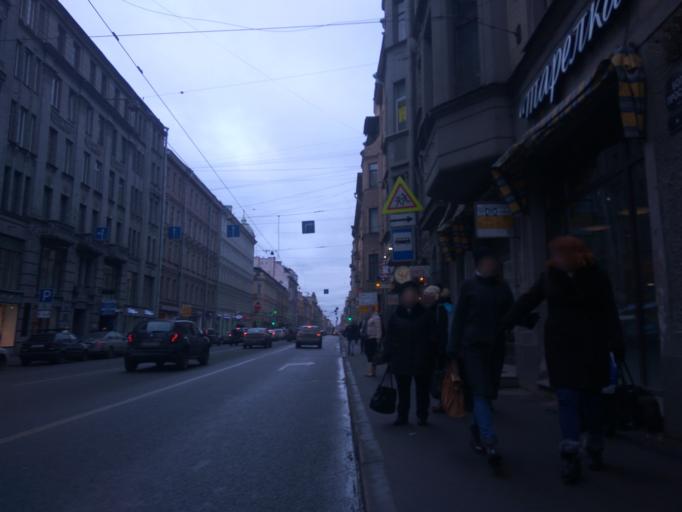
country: RU
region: St.-Petersburg
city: Petrogradka
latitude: 59.9642
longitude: 30.3096
